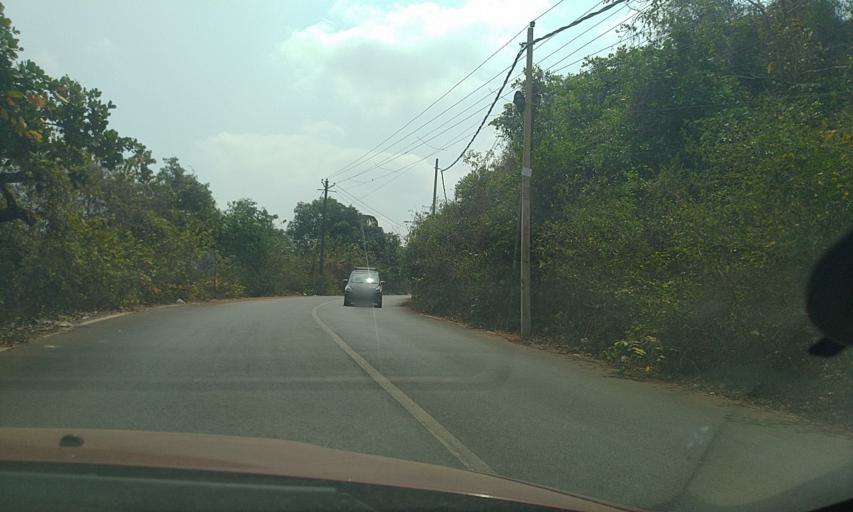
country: IN
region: Goa
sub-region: North Goa
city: Mapuca
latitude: 15.5967
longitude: 73.7930
